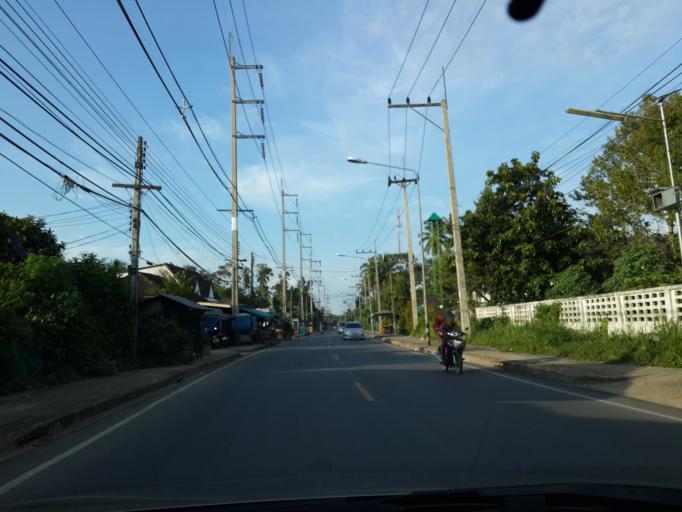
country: TH
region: Yala
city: Yala
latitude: 6.5294
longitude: 101.2622
